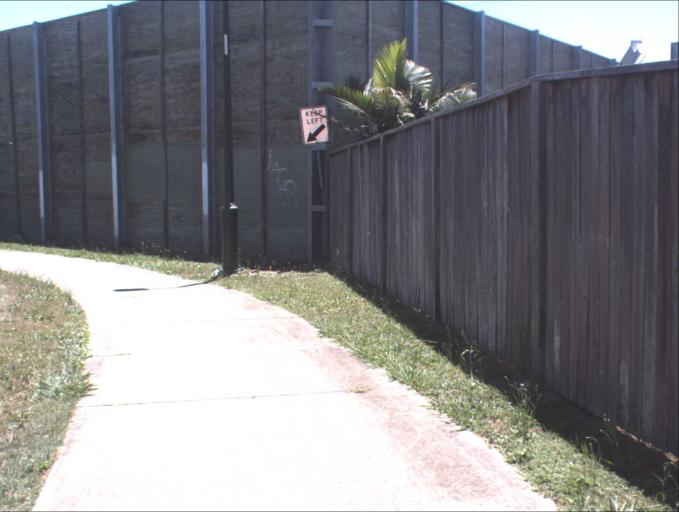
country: AU
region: Queensland
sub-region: Logan
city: Beenleigh
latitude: -27.6820
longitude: 153.1866
